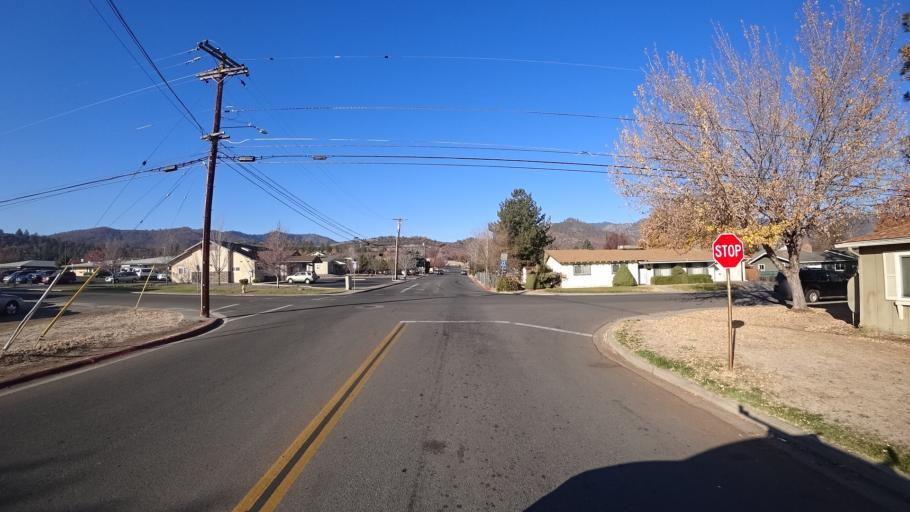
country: US
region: California
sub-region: Siskiyou County
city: Yreka
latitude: 41.7185
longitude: -122.6416
